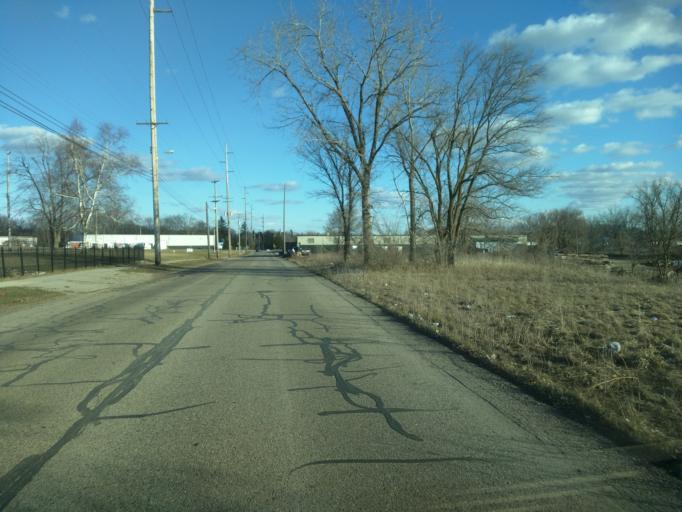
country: US
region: Michigan
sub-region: Ingham County
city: Edgemont Park
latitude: 42.7633
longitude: -84.5660
